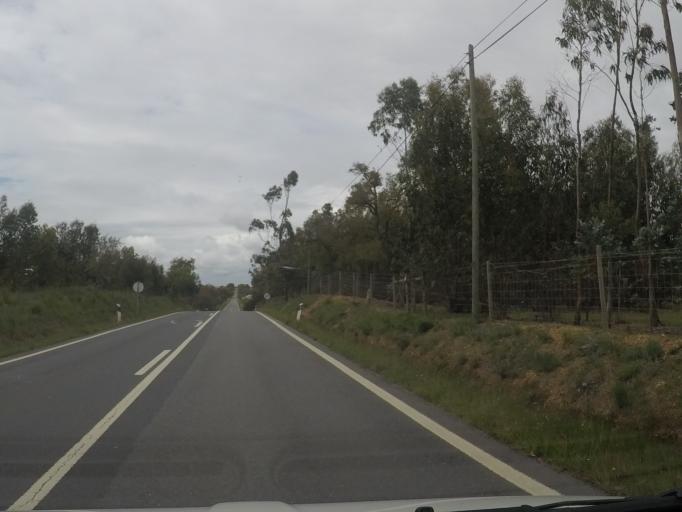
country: PT
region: Setubal
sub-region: Santiago do Cacem
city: Cercal
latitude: 37.8553
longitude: -8.7132
